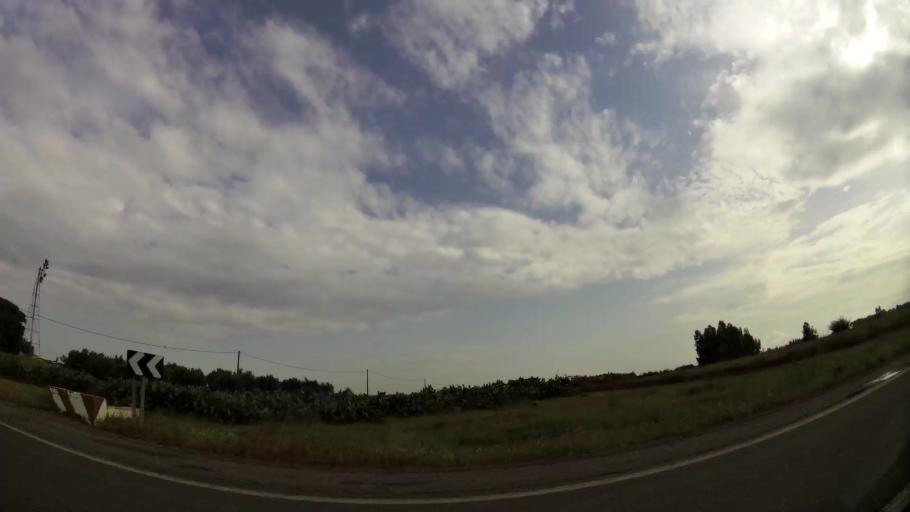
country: MA
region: Rabat-Sale-Zemmour-Zaer
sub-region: Khemisset
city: Khemisset
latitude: 33.7939
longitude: -6.1100
